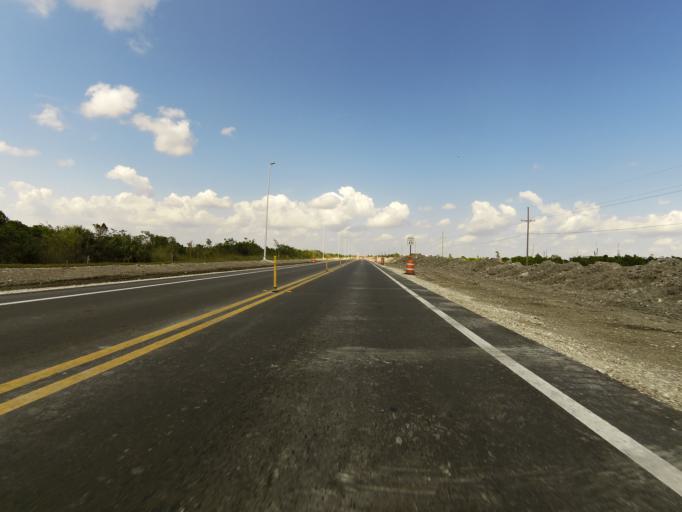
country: US
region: Florida
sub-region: Miami-Dade County
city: Doral
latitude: 25.9007
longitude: -80.4767
